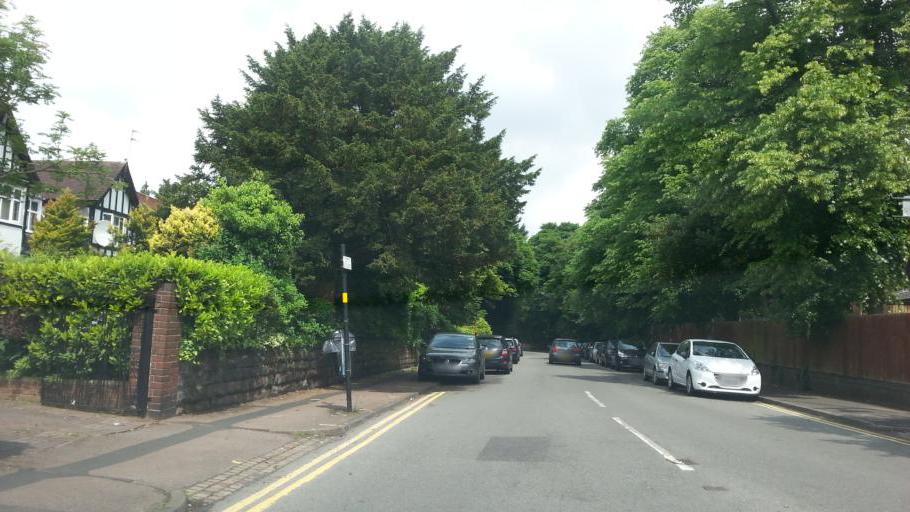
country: GB
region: England
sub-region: City and Borough of Birmingham
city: Birmingham
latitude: 52.4462
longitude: -1.8843
